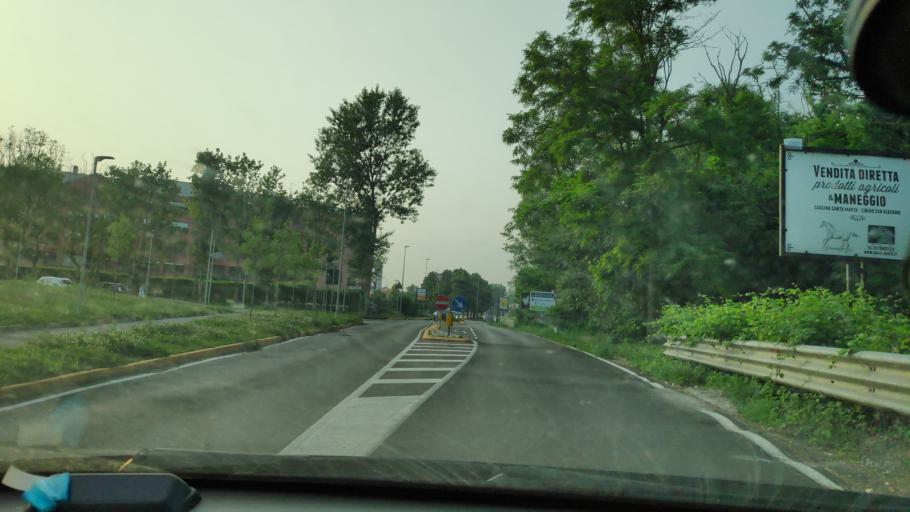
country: IT
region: Lombardy
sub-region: Citta metropolitana di Milano
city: Basiglio
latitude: 45.3711
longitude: 9.1485
